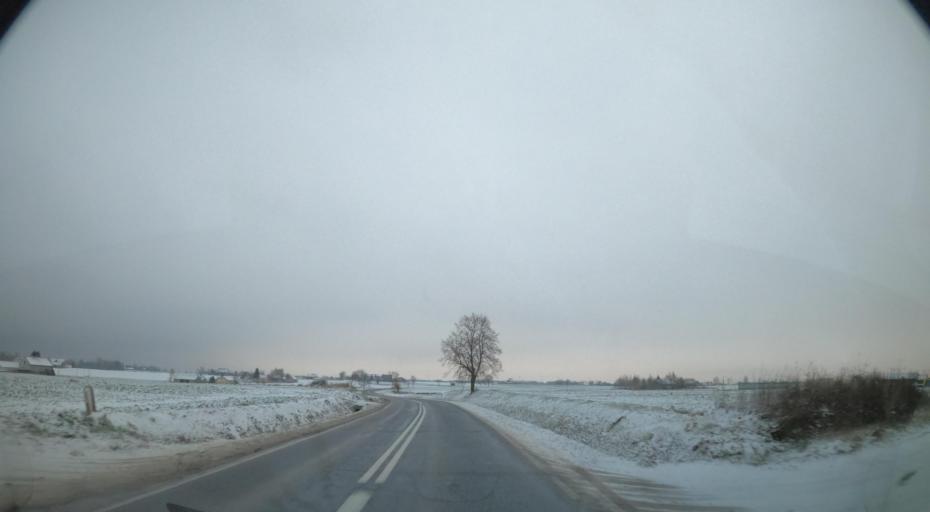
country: PL
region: Kujawsko-Pomorskie
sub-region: Powiat lipnowski
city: Dobrzyn nad Wisla
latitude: 52.6359
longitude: 19.4060
